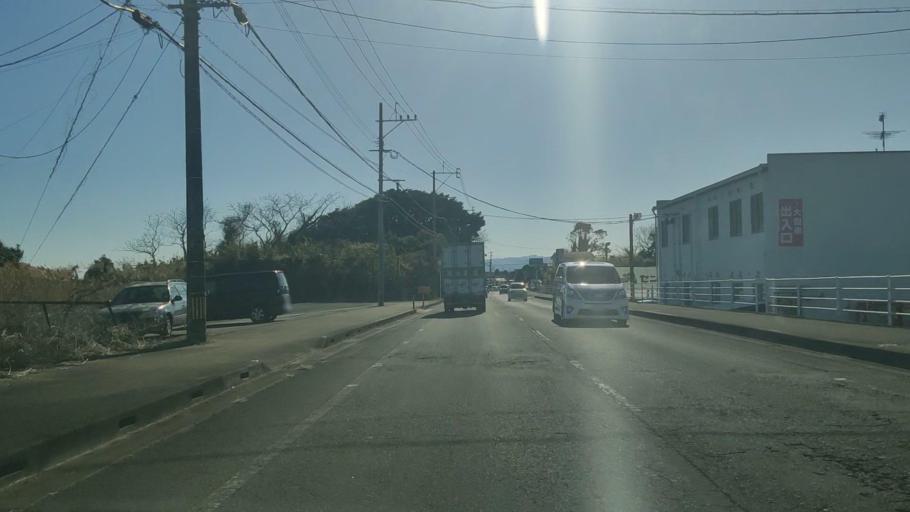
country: JP
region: Miyazaki
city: Miyazaki-shi
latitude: 31.9451
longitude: 131.4586
